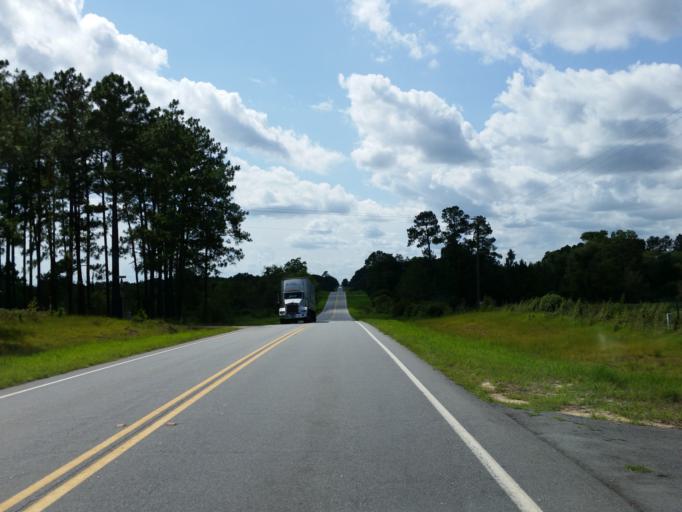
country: US
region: Georgia
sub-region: Turner County
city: Ashburn
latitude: 31.6455
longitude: -83.5357
